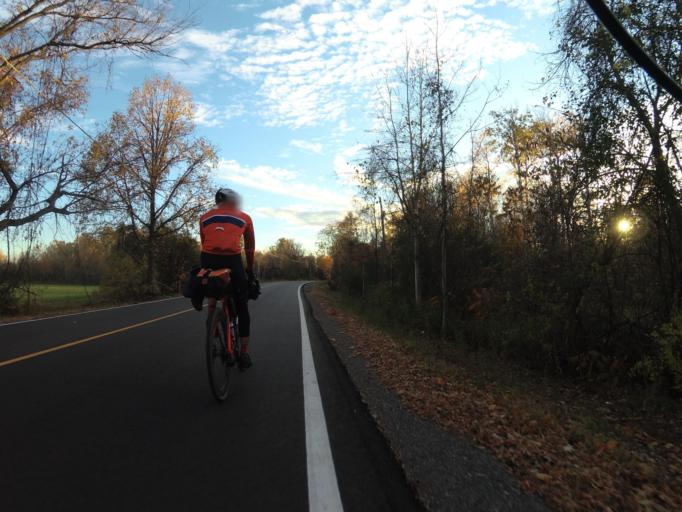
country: CA
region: Ontario
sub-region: Lanark County
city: Smiths Falls
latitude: 44.9474
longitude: -75.8178
